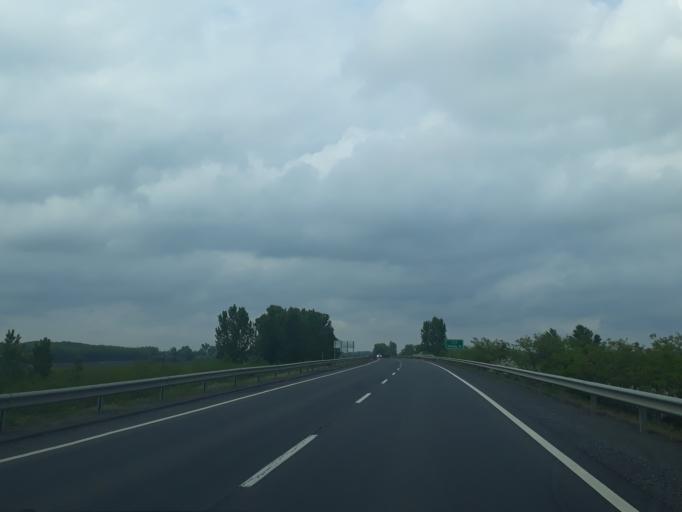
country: HU
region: Szabolcs-Szatmar-Bereg
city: Ajak
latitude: 48.1818
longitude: 22.0422
